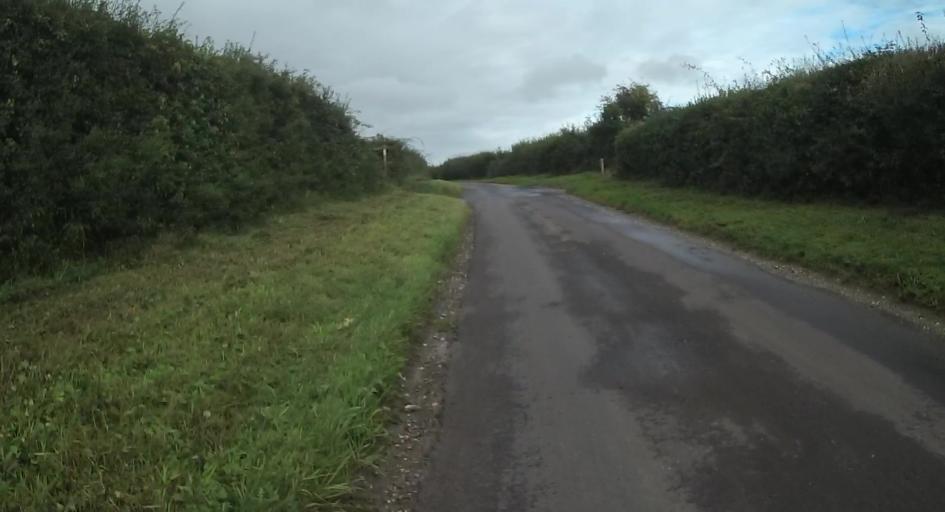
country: GB
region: England
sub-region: Hampshire
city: Basingstoke
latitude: 51.2814
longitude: -1.1450
